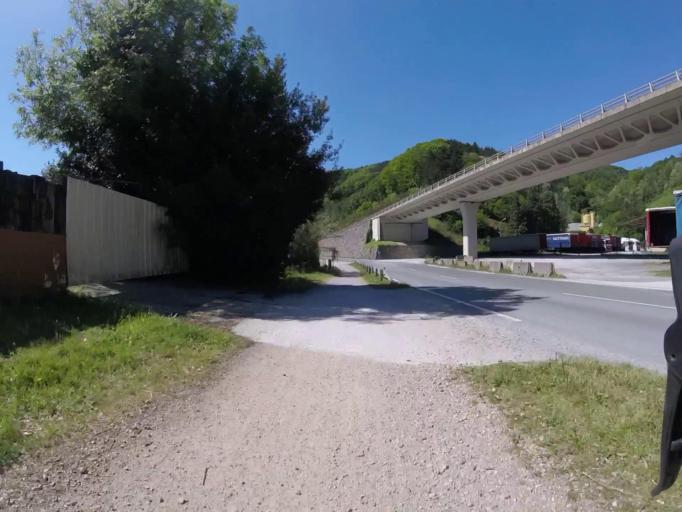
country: ES
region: Basque Country
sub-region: Provincia de Guipuzcoa
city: Irun
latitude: 43.3218
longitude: -1.7417
